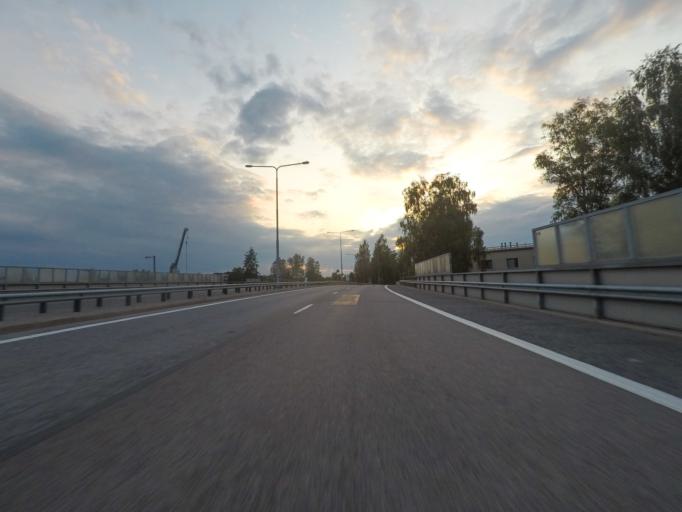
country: FI
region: Central Finland
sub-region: Jyvaeskylae
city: Jyvaeskylae
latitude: 62.2465
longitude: 25.7655
